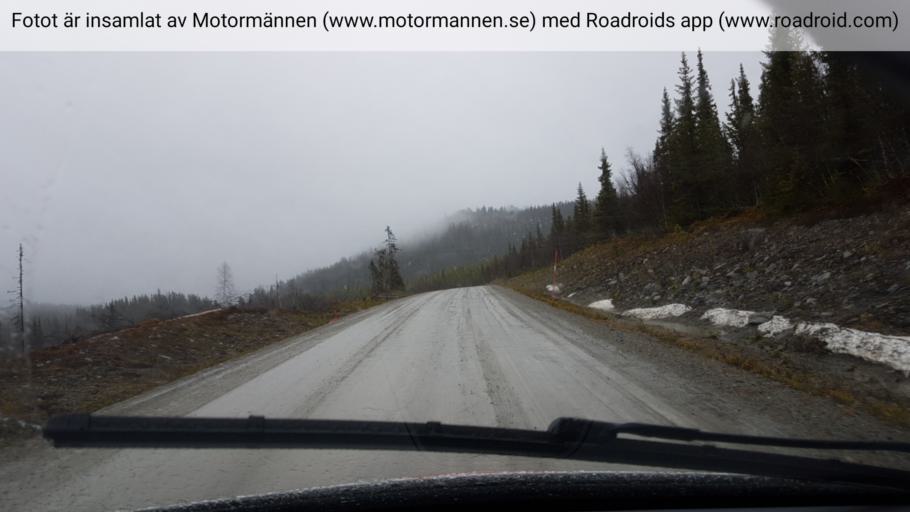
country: SE
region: Jaemtland
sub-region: Are Kommun
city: Are
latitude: 62.6320
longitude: 13.1060
